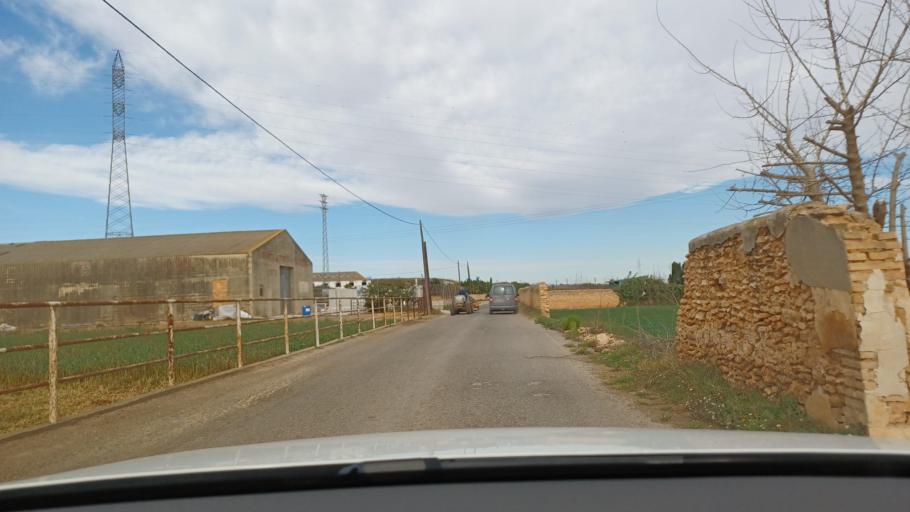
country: ES
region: Valencia
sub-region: Provincia de Valencia
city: Benifaio
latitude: 39.2893
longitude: -0.4343
